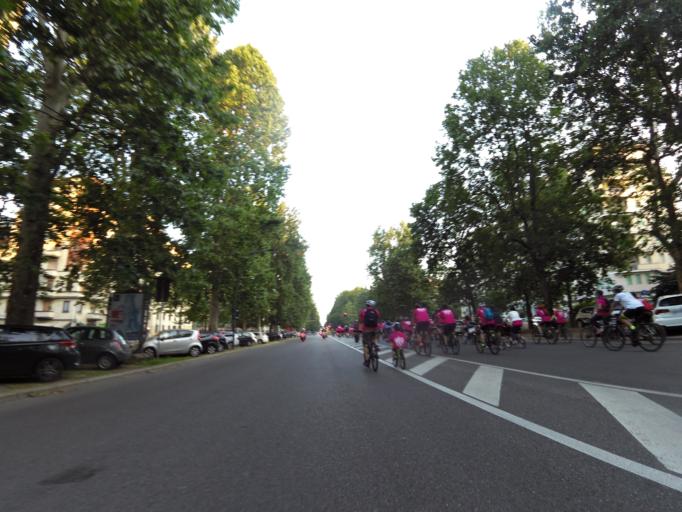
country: IT
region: Lombardy
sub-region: Citta metropolitana di Milano
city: Milano
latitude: 45.4815
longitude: 9.1647
